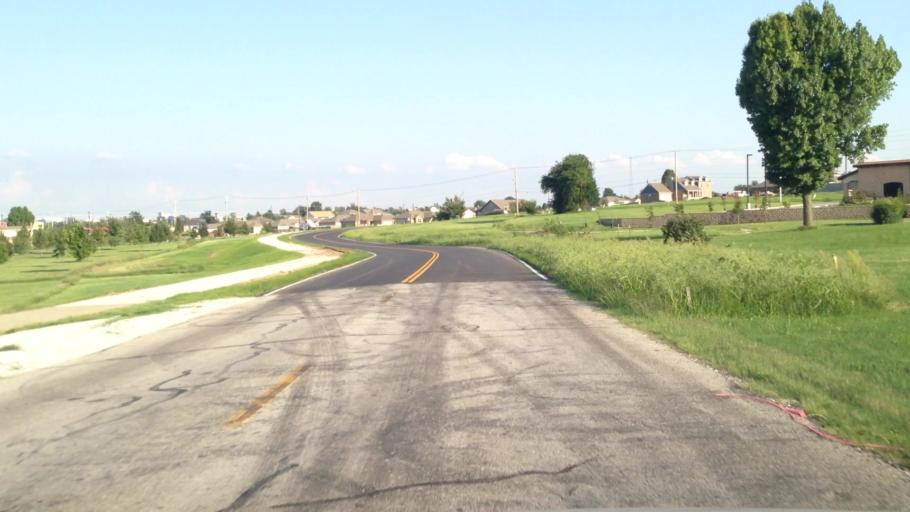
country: US
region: Missouri
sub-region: Jasper County
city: Duquesne
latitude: 37.0709
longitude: -94.4864
